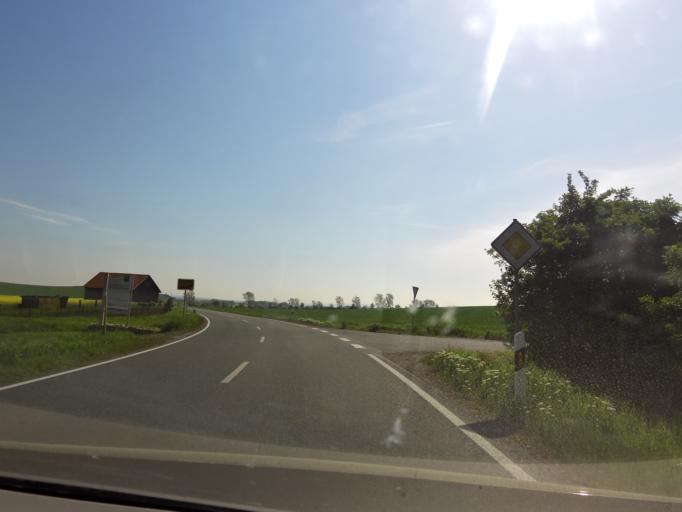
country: DE
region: Thuringia
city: Witterda
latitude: 51.0385
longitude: 10.8968
